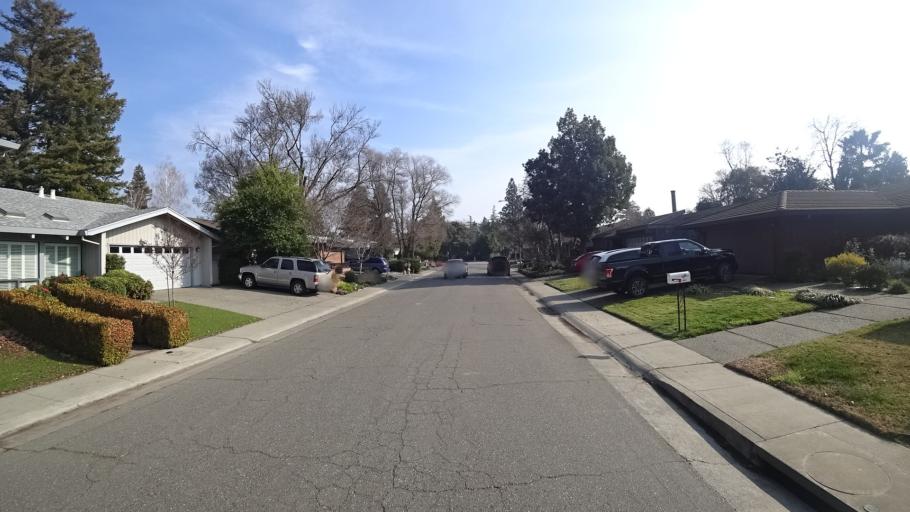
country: US
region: California
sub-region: Yolo County
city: Davis
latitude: 38.5657
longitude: -121.7598
